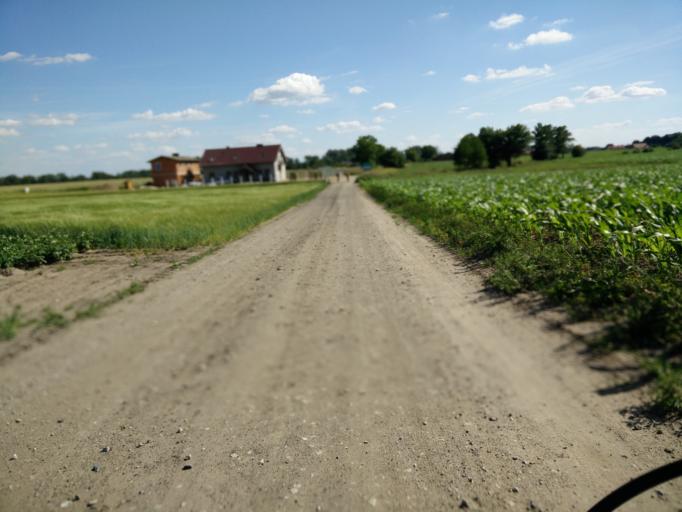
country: PL
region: Greater Poland Voivodeship
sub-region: Powiat sredzki
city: Dominowo
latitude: 52.2601
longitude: 17.3204
